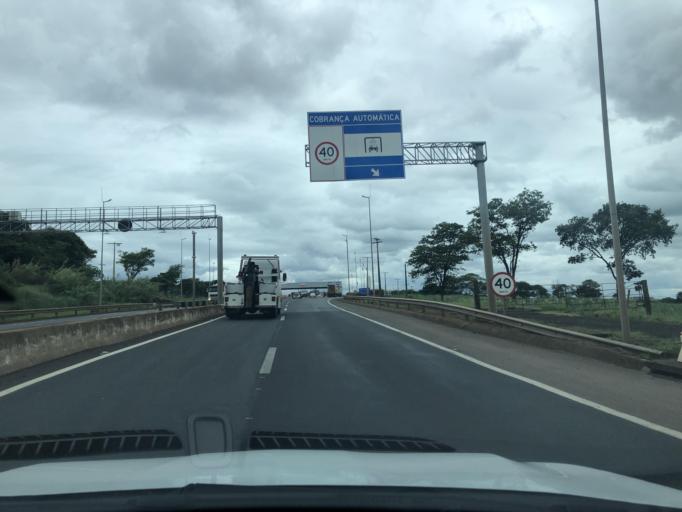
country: BR
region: Sao Paulo
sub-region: Igarapava
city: Igarapava
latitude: -19.9131
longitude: -47.8312
